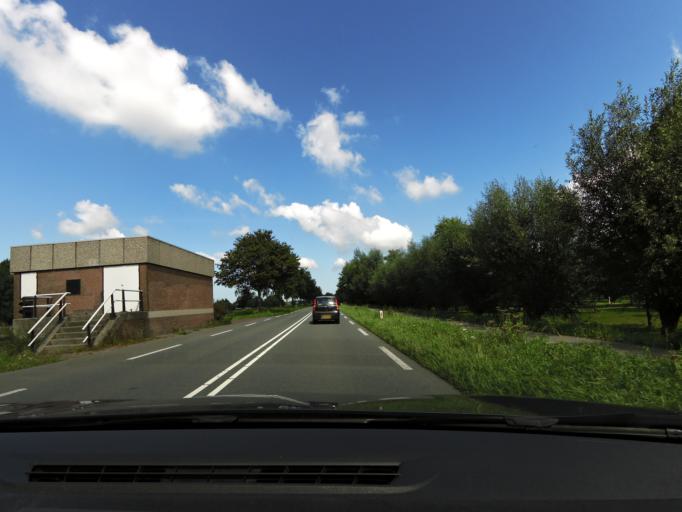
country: NL
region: South Holland
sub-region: Gemeente Alphen aan den Rijn
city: Alphen aan den Rijn
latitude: 52.1495
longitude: 4.7054
